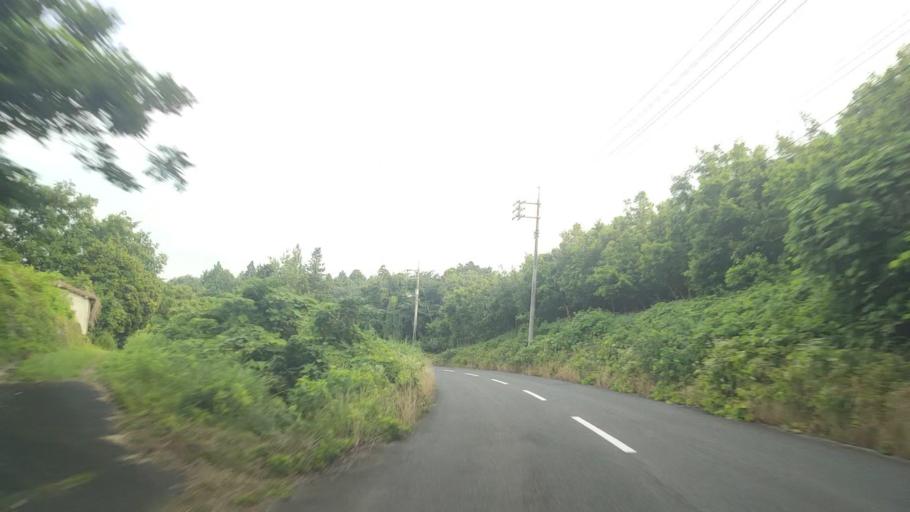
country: JP
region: Tottori
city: Kurayoshi
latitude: 35.3977
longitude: 133.7732
